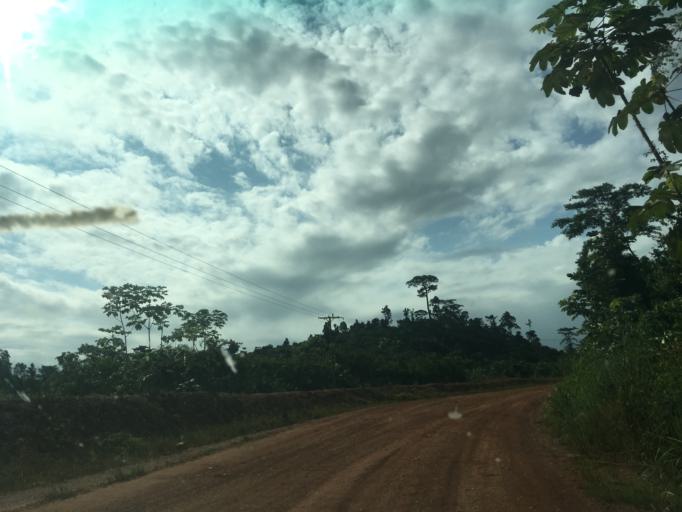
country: GH
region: Western
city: Wassa-Akropong
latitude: 5.9191
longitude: -2.4067
